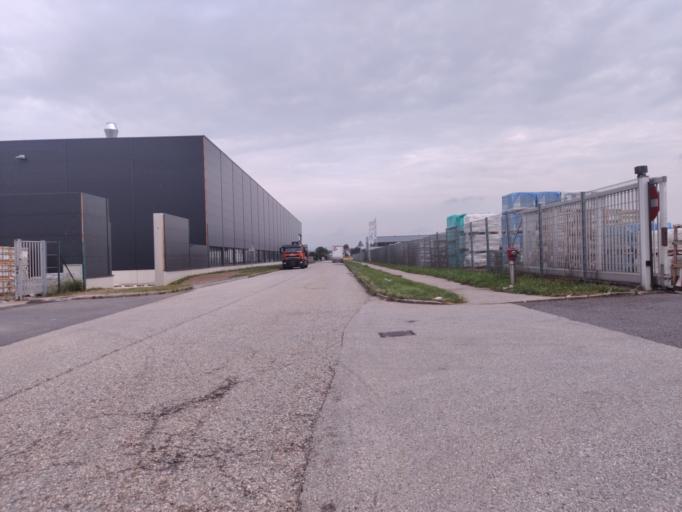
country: AT
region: Lower Austria
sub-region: Politischer Bezirk Amstetten
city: Ennsdorf
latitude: 48.2220
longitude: 14.5075
